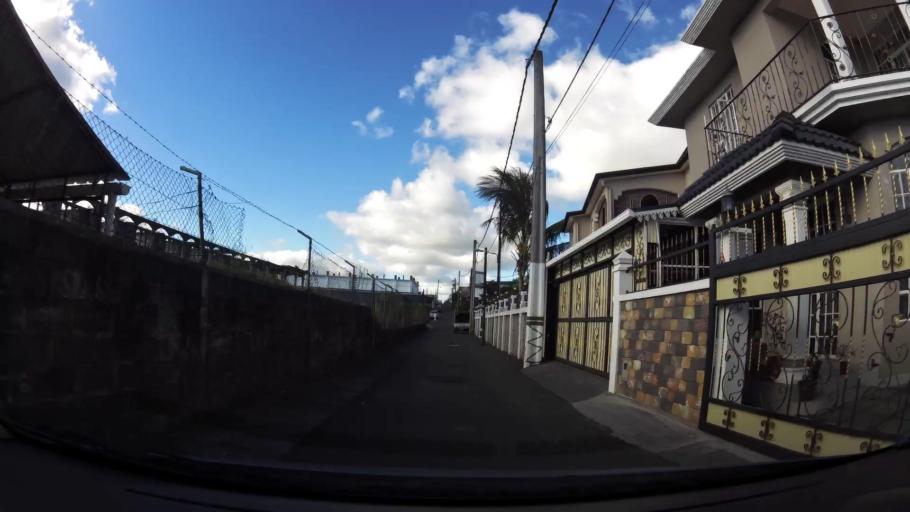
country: MU
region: Plaines Wilhems
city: Vacoas
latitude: -20.2937
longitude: 57.4838
